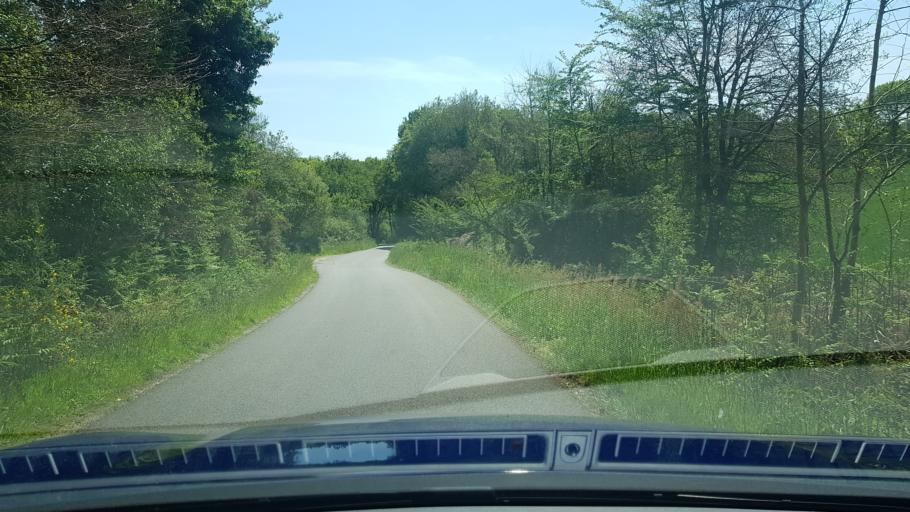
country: FR
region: Brittany
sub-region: Departement du Morbihan
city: Pont-Scorff
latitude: 47.8174
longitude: -3.4181
